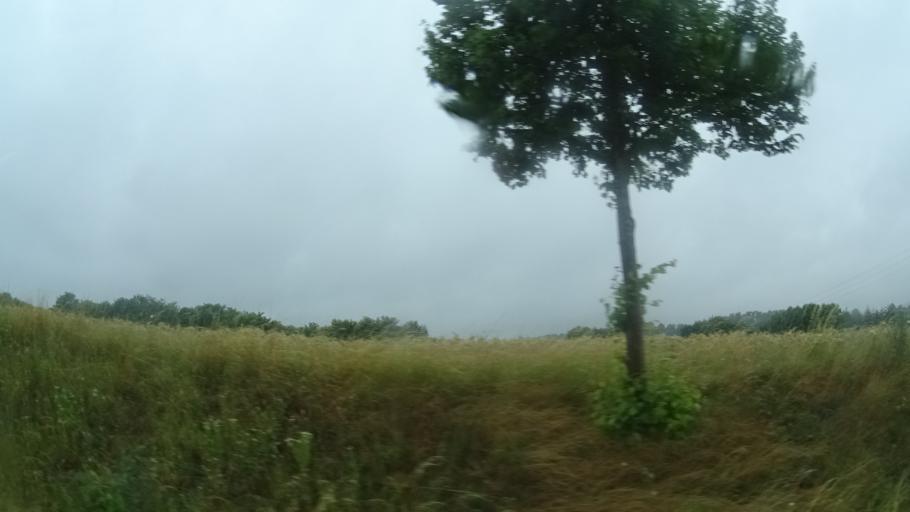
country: DE
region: Rheinland-Pfalz
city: Gries
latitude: 49.4159
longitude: 7.4257
